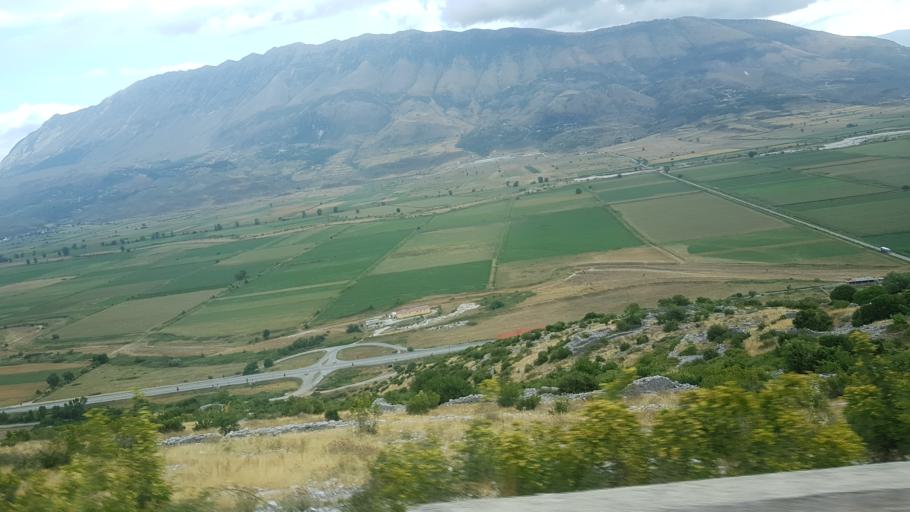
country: AL
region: Gjirokaster
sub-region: Rrethi i Gjirokastres
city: Libohove
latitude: 39.9479
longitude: 20.2501
